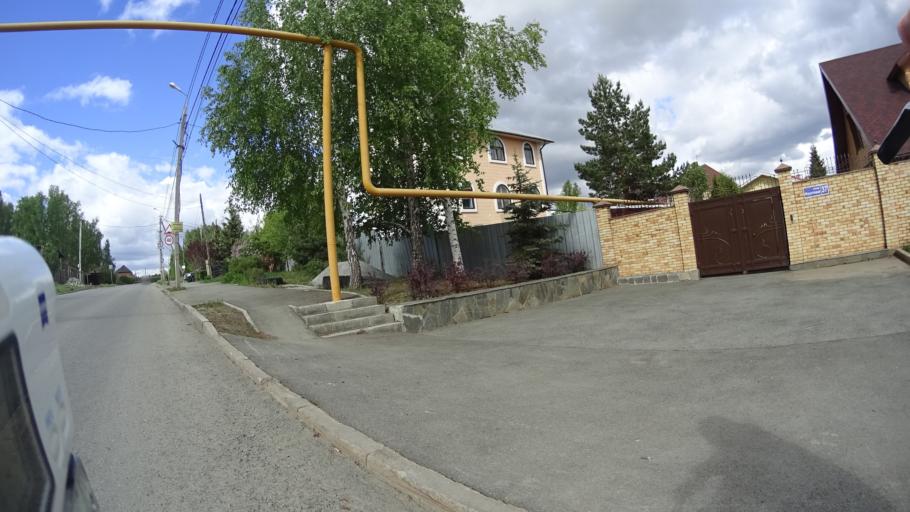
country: RU
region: Chelyabinsk
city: Sargazy
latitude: 55.1572
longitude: 61.2519
